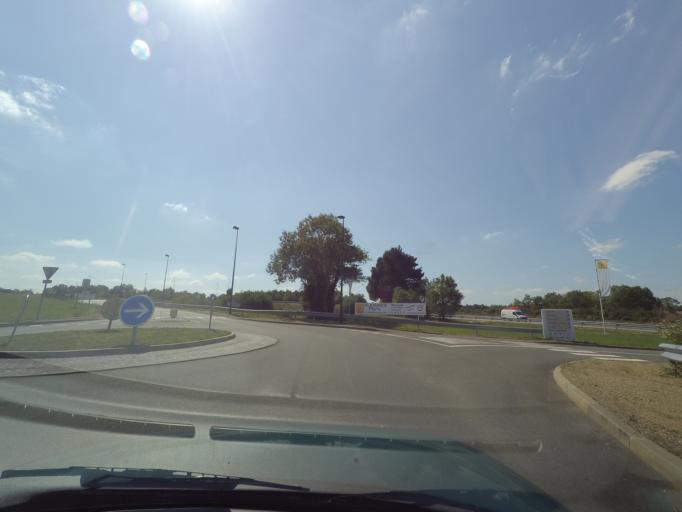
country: FR
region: Pays de la Loire
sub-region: Departement de la Loire-Atlantique
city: Saint-Philbert-de-Grand-Lieu
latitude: 47.0347
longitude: -1.6548
